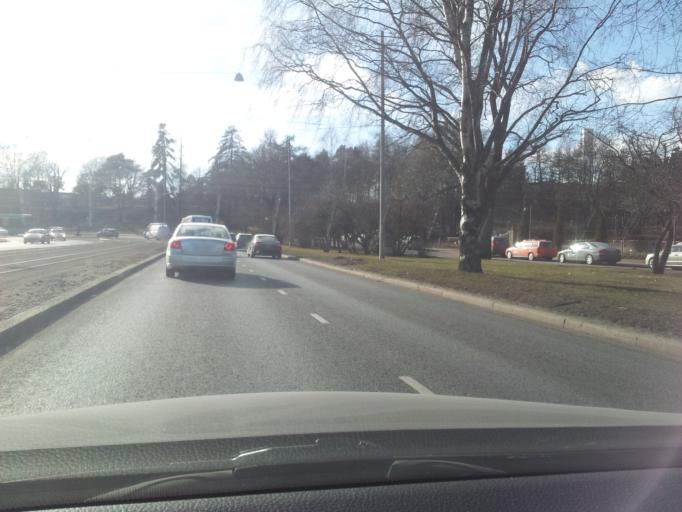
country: FI
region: Uusimaa
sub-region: Helsinki
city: Helsinki
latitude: 60.1849
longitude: 24.9338
